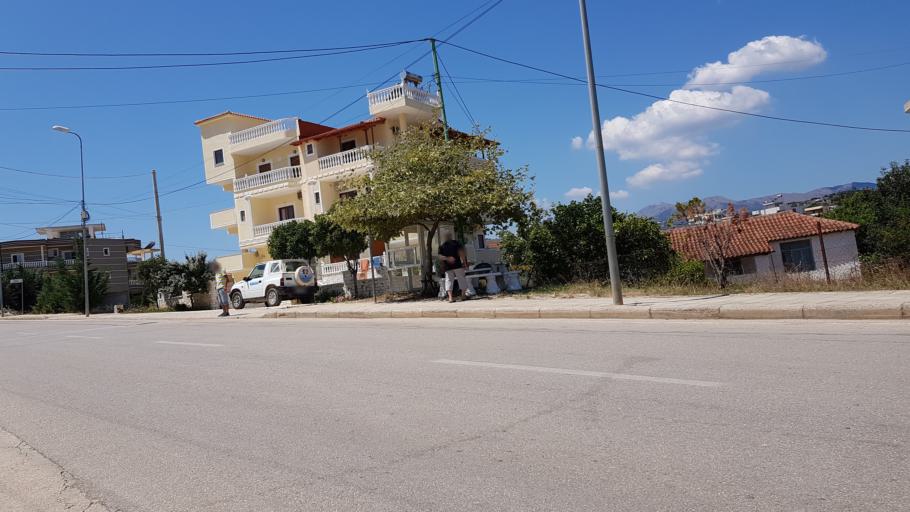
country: AL
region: Vlore
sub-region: Rrethi i Sarandes
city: Xarre
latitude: 39.7667
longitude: 20.0021
